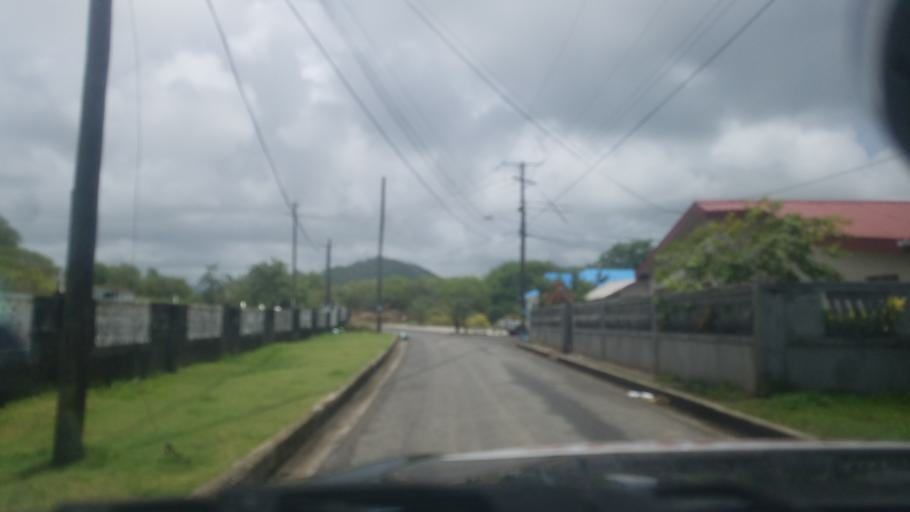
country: LC
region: Vieux-Fort
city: Vieux Fort
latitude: 13.7383
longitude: -60.9575
